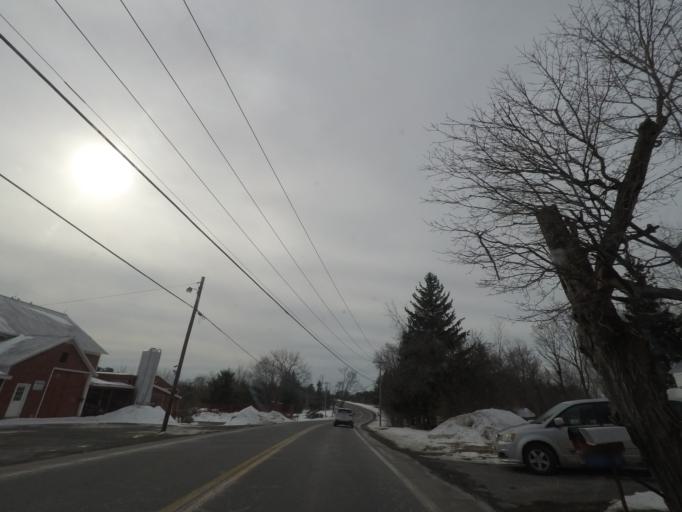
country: US
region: New York
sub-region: Albany County
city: Altamont
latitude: 42.6774
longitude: -74.1044
